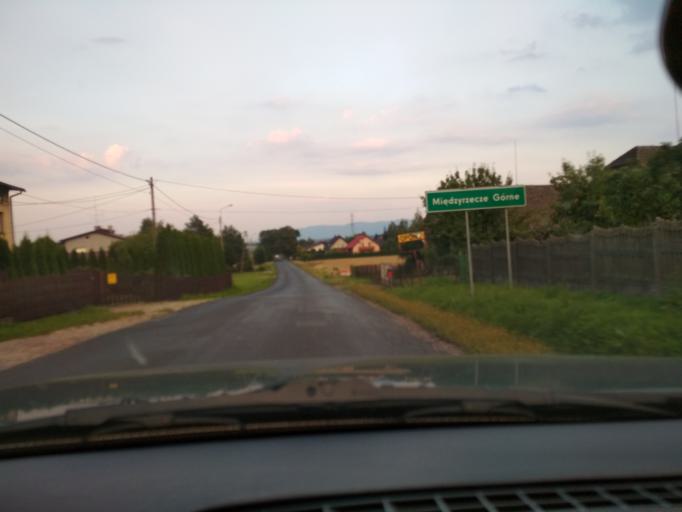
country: PL
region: Silesian Voivodeship
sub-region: Powiat bielski
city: Bronow
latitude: 49.8571
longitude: 18.9140
